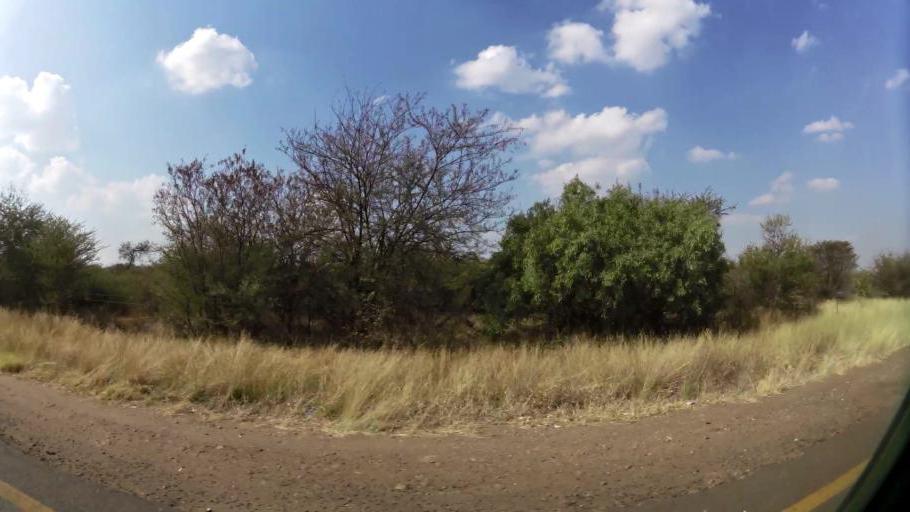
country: ZA
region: North-West
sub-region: Bojanala Platinum District Municipality
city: Mogwase
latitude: -25.4468
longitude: 27.0880
